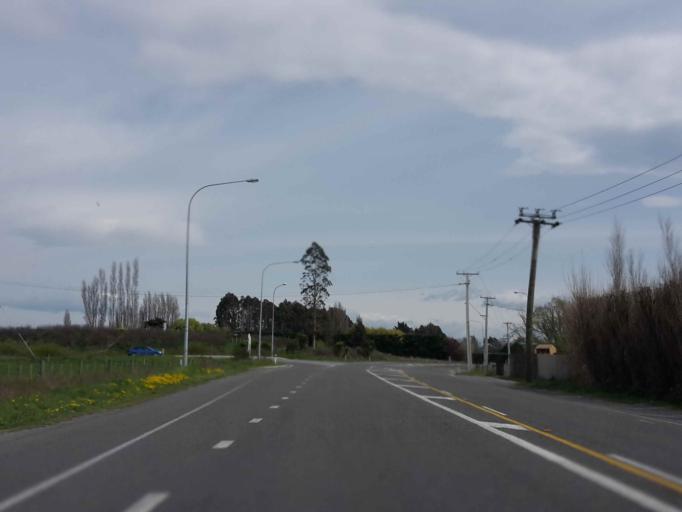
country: NZ
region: Canterbury
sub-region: Waimakariri District
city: Kaiapoi
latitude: -43.4033
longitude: 172.6165
